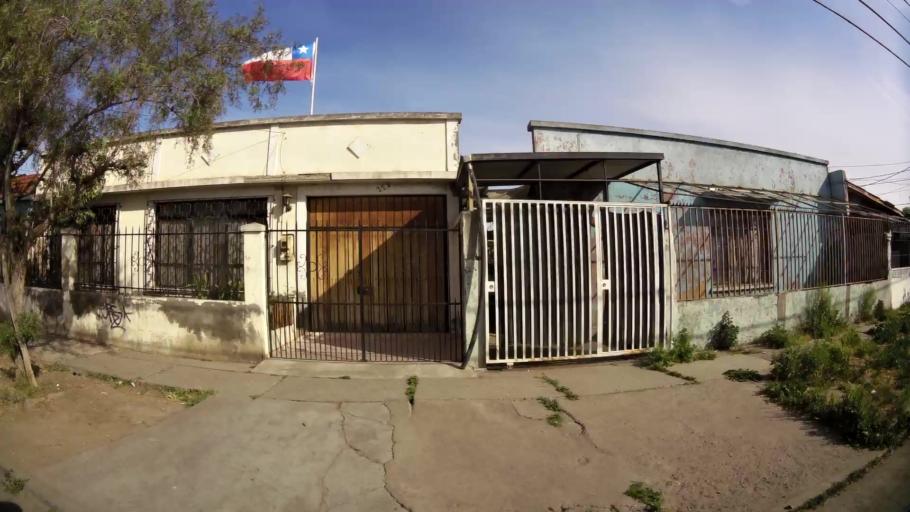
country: CL
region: Santiago Metropolitan
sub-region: Provincia de Santiago
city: La Pintana
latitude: -33.5230
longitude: -70.6234
